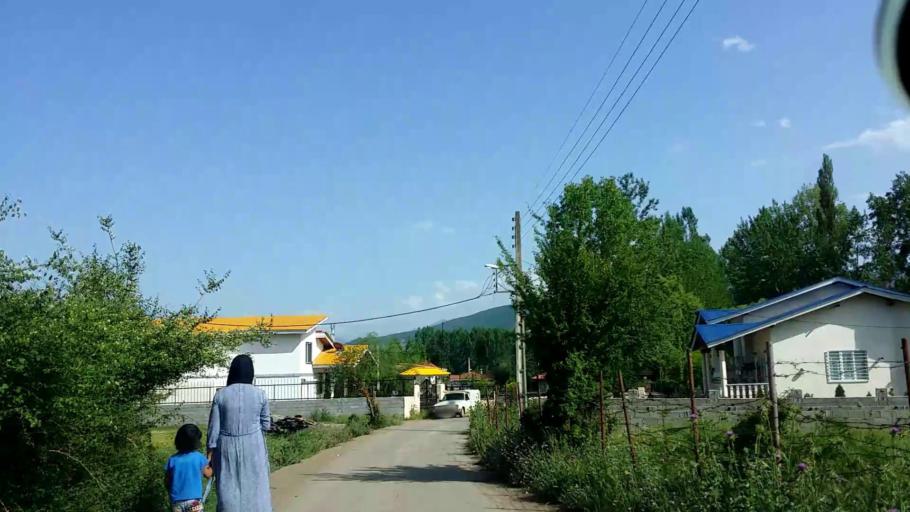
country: IR
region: Mazandaran
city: `Abbasabad
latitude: 36.5373
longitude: 51.1952
